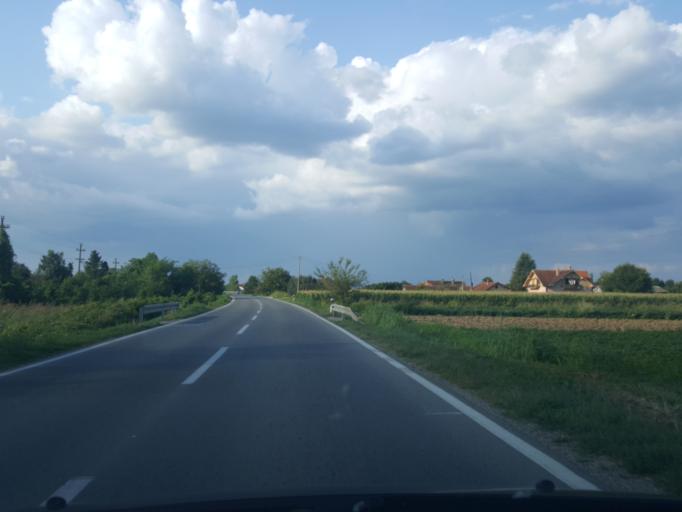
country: RS
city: Kozjak
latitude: 44.6281
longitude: 19.2723
